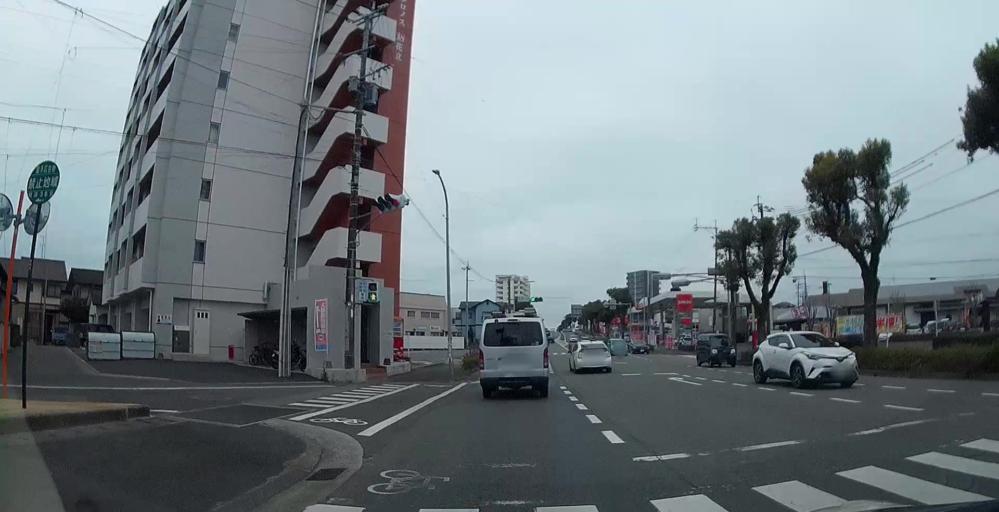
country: JP
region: Kumamoto
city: Kumamoto
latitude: 32.7897
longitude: 130.7771
